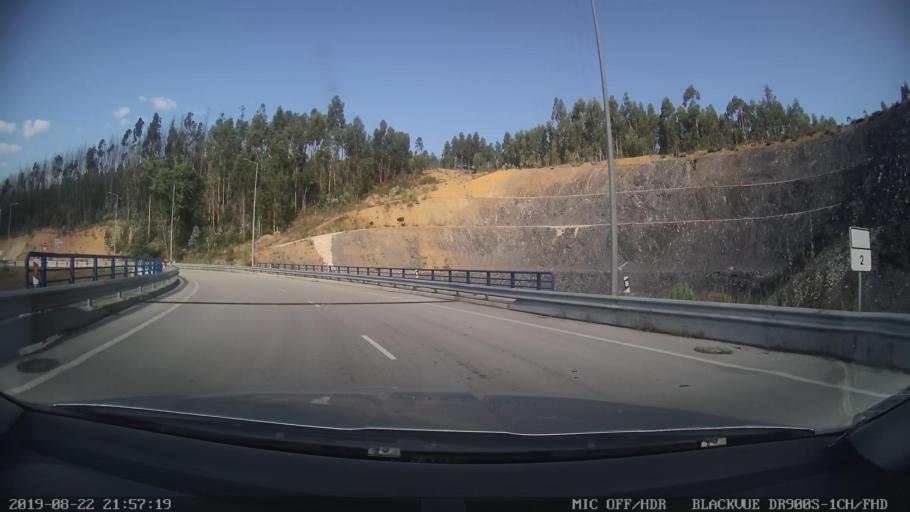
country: PT
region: Coimbra
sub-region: Coimbra
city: Coimbra
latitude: 40.1832
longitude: -8.3790
